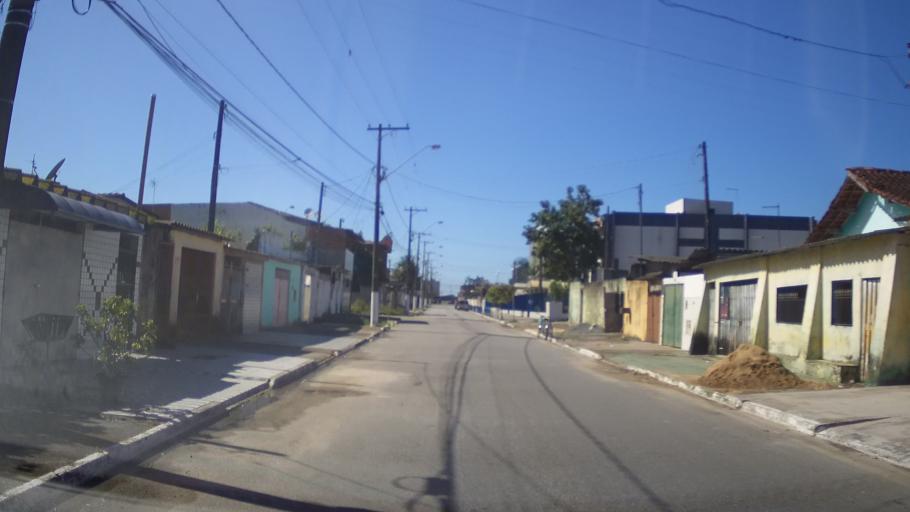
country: BR
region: Sao Paulo
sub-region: Praia Grande
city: Praia Grande
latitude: -24.0328
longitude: -46.5161
